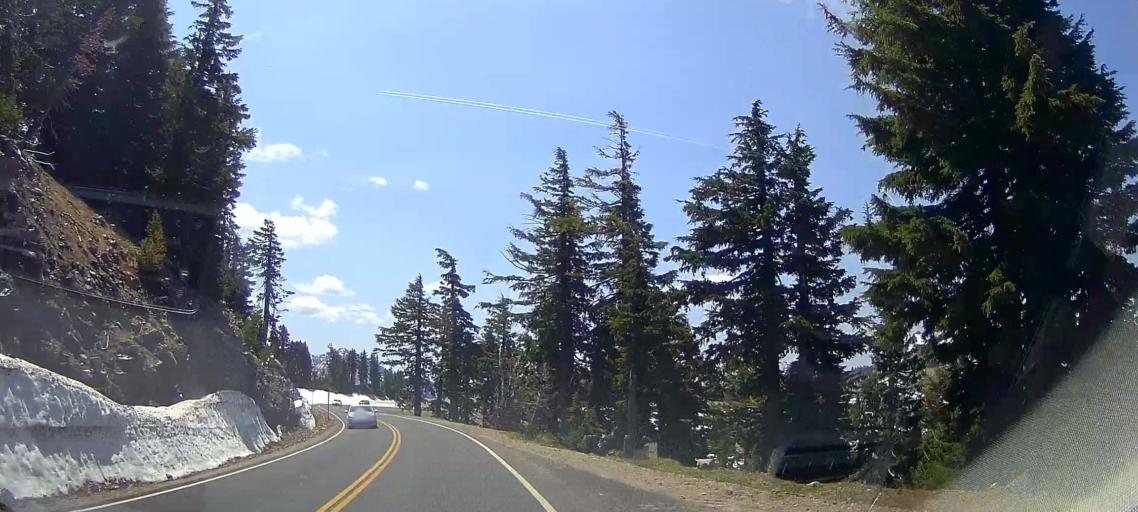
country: US
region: Oregon
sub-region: Jackson County
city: Shady Cove
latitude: 42.9691
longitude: -122.1500
